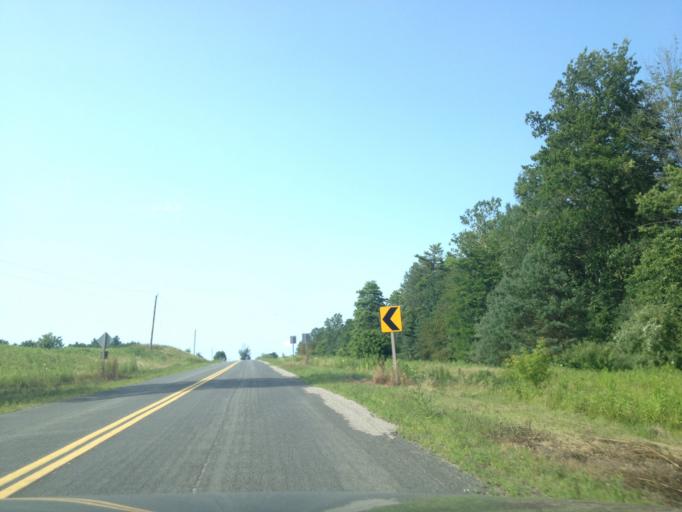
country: CA
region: Ontario
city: Aylmer
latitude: 42.7337
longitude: -80.8536
